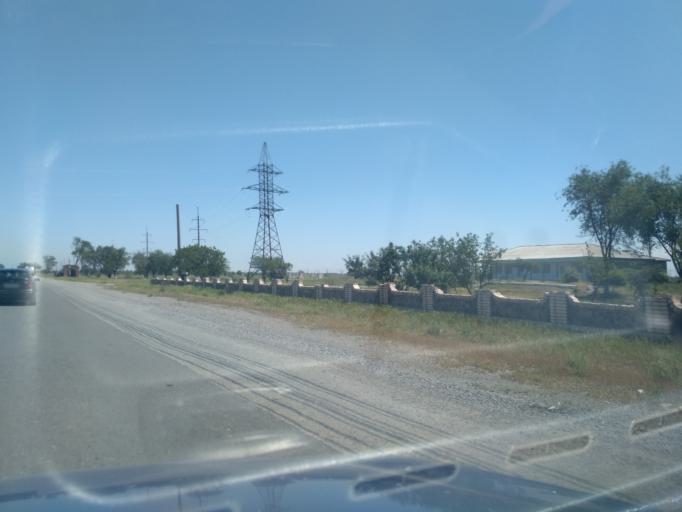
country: TJ
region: Viloyati Sughd
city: Zafarobod
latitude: 40.2169
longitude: 68.8895
